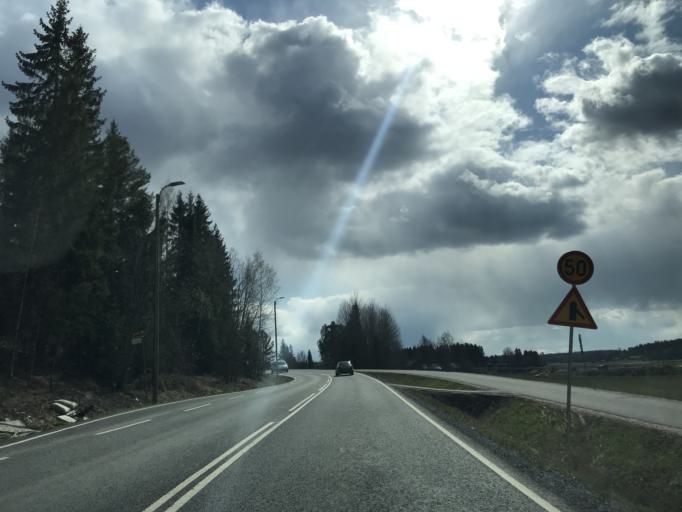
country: FI
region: Uusimaa
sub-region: Helsinki
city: Jaervenpaeae
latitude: 60.4838
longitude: 25.0428
